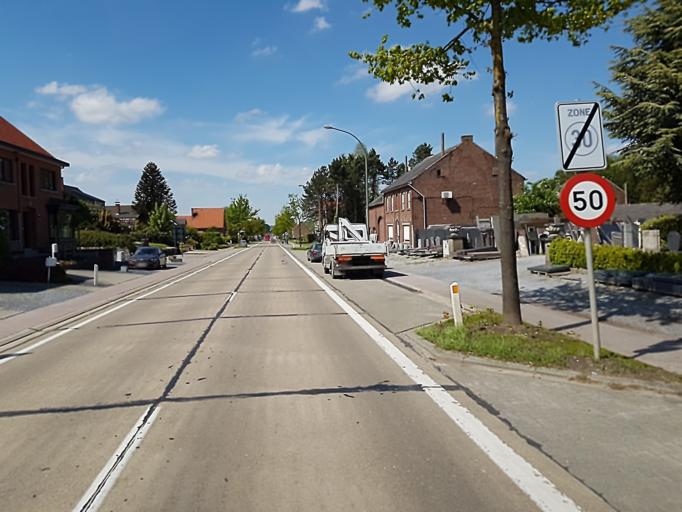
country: BE
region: Flanders
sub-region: Provincie Vlaams-Brabant
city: Tienen
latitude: 50.8383
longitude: 4.9171
